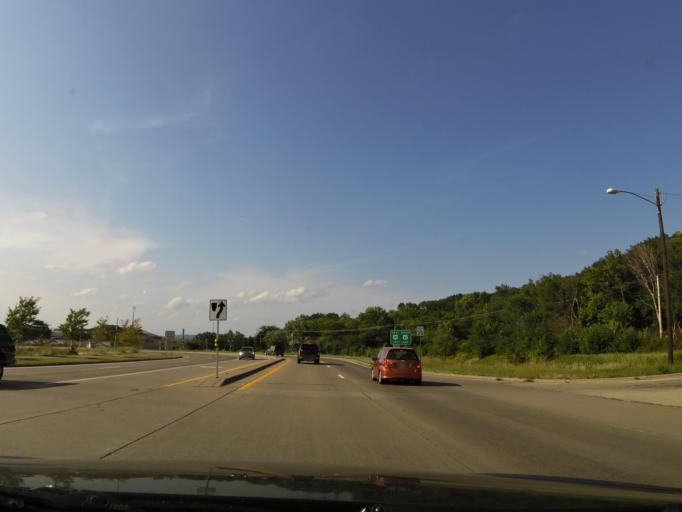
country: US
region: Minnesota
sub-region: Washington County
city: Newport
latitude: 44.8901
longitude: -93.0047
